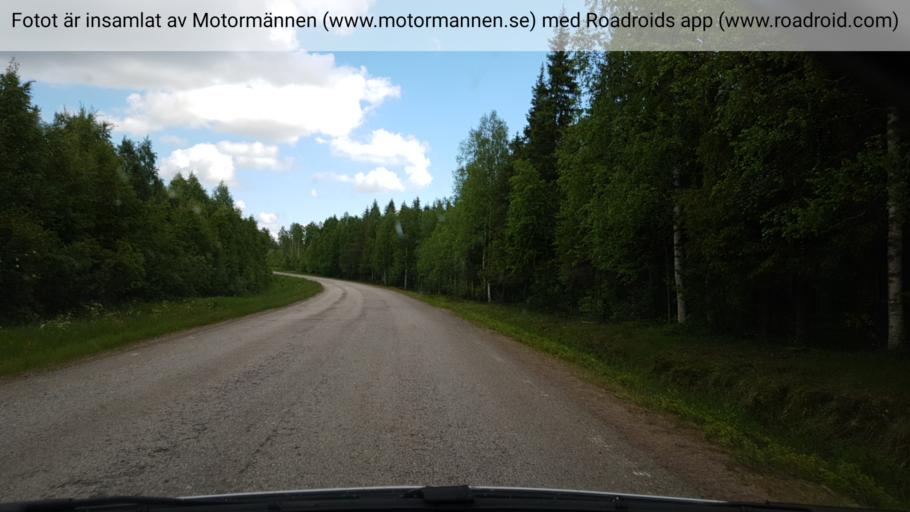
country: FI
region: Lapland
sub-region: Torniolaakso
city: Ylitornio
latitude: 66.1846
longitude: 23.7309
